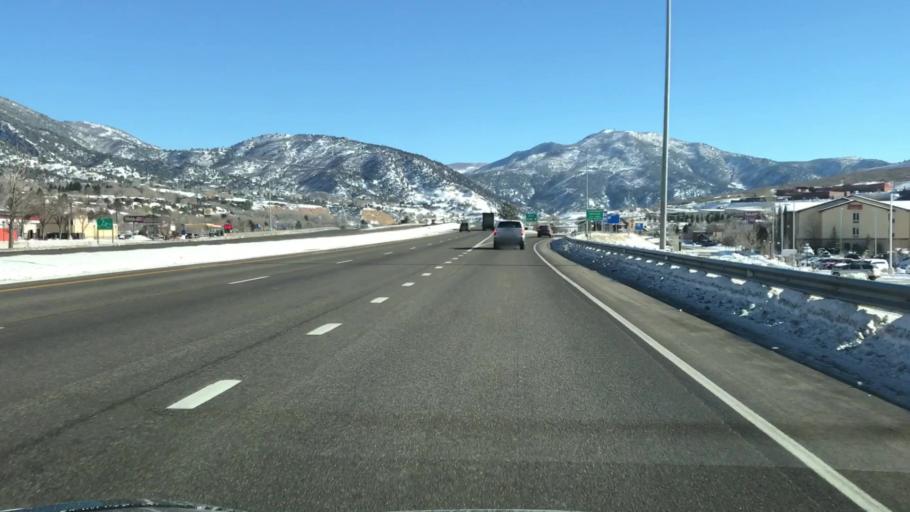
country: US
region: Colorado
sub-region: Garfield County
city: Glenwood Springs
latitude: 39.5613
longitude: -107.3659
